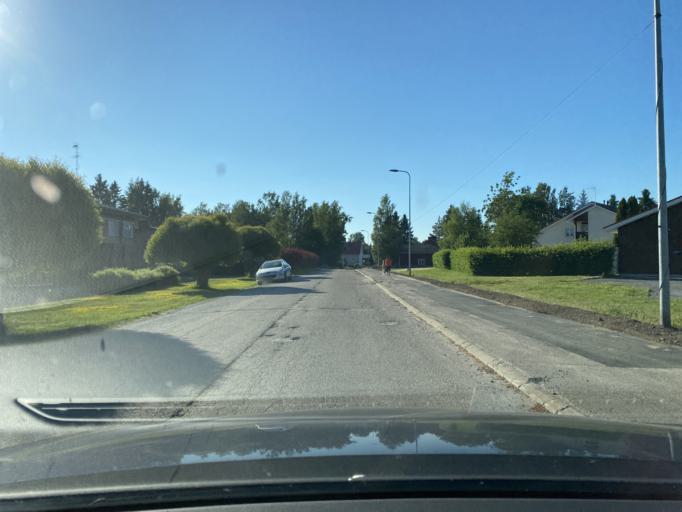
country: FI
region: Satakunta
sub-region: Pori
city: Huittinen
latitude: 61.1696
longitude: 22.7008
